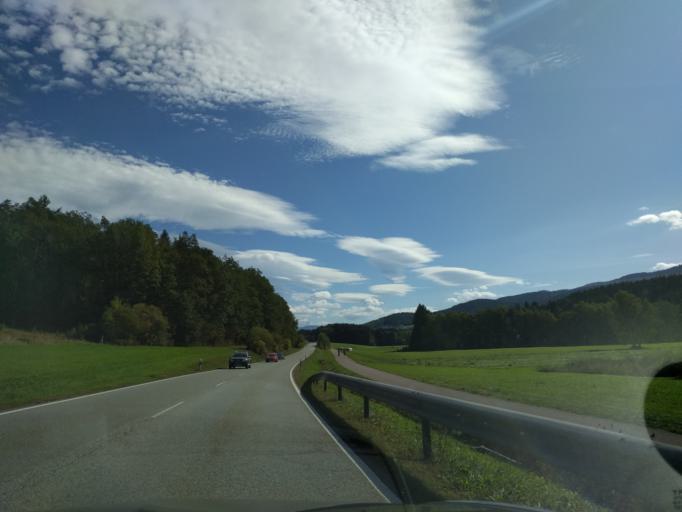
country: DE
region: Bavaria
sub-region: Upper Palatinate
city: Grafenwiesen
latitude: 49.2102
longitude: 12.8952
